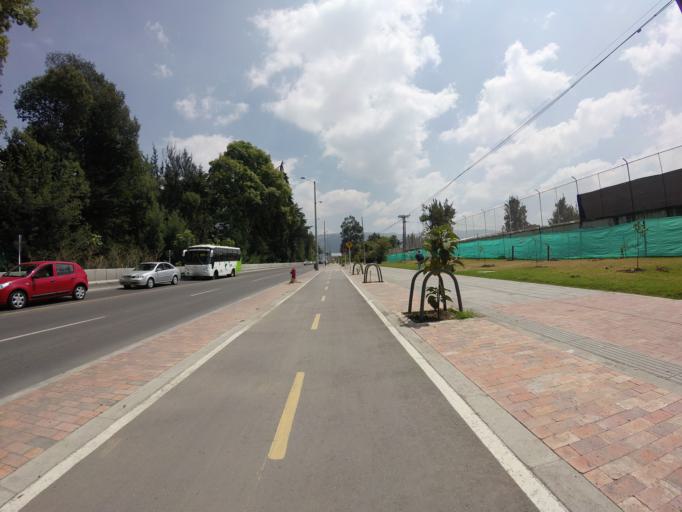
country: CO
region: Bogota D.C.
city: Barrio San Luis
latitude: 4.7388
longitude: -74.0538
